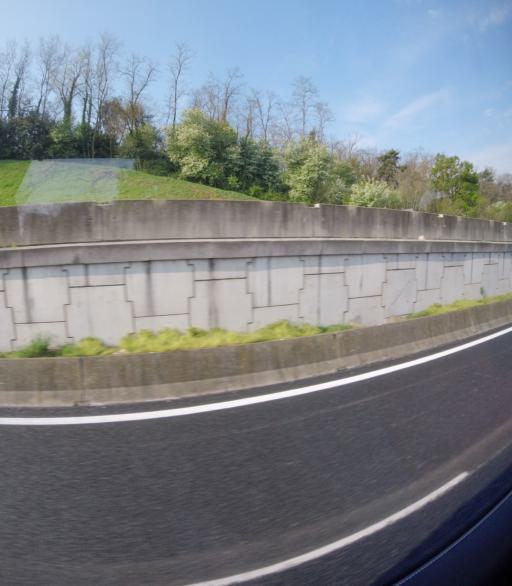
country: IT
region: Piedmont
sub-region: Provincia di Novara
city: Borgo Ticino
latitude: 45.7042
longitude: 8.6022
